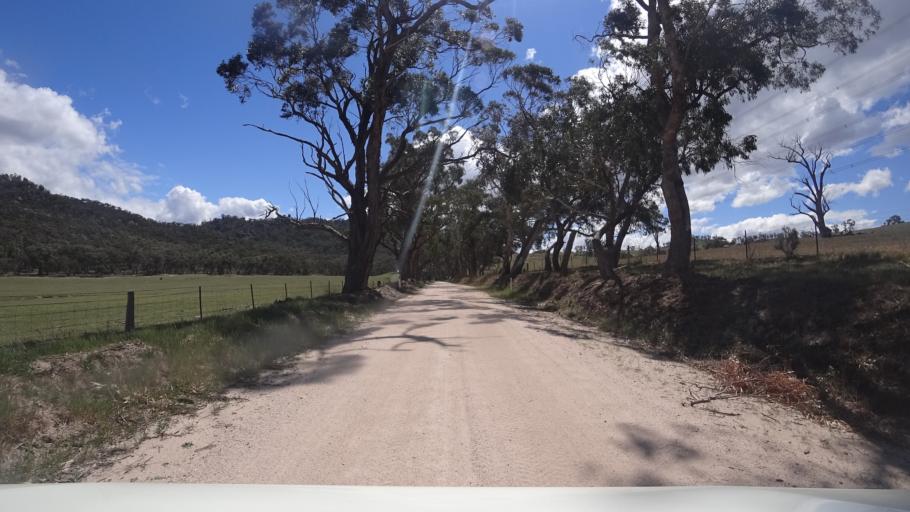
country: AU
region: New South Wales
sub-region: Oberon
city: Oberon
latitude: -33.5558
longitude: 149.9329
